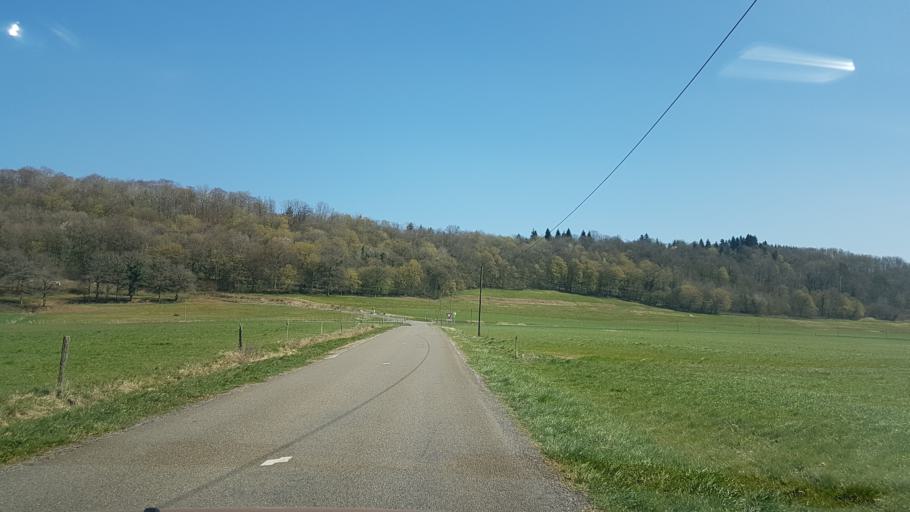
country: FR
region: Franche-Comte
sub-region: Departement du Jura
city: Orgelet
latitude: 46.5095
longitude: 5.5315
